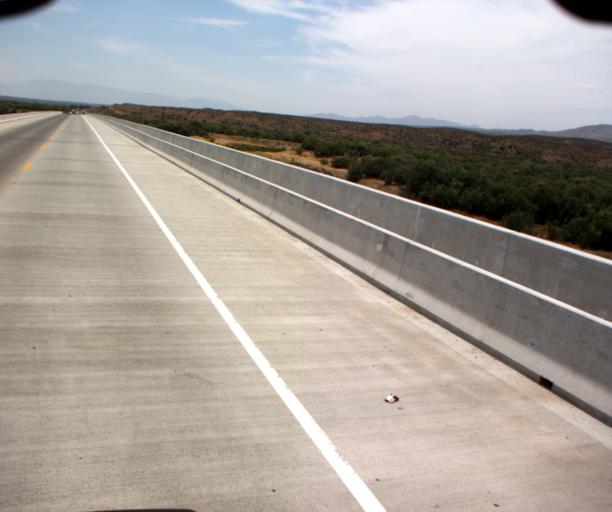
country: US
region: Arizona
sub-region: Graham County
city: Bylas
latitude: 33.1658
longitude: -110.1345
